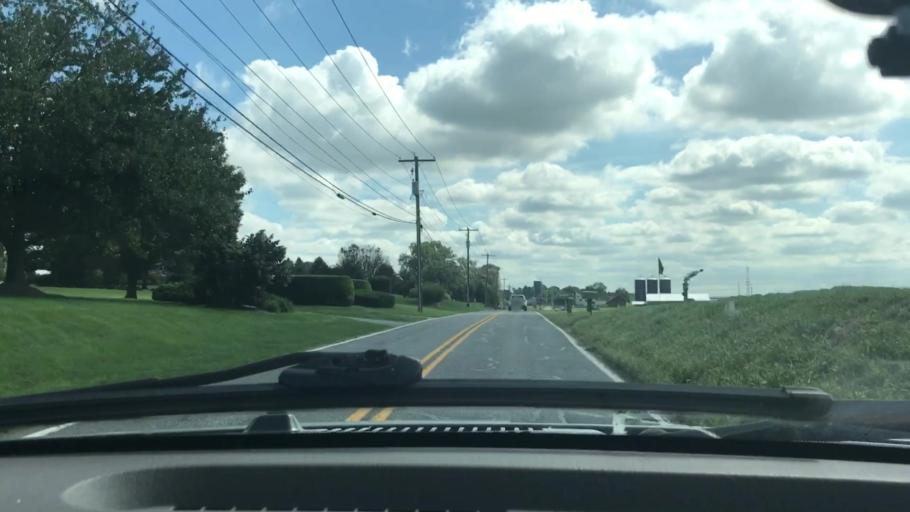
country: US
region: Pennsylvania
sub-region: Lancaster County
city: East Petersburg
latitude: 40.0969
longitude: -76.3806
